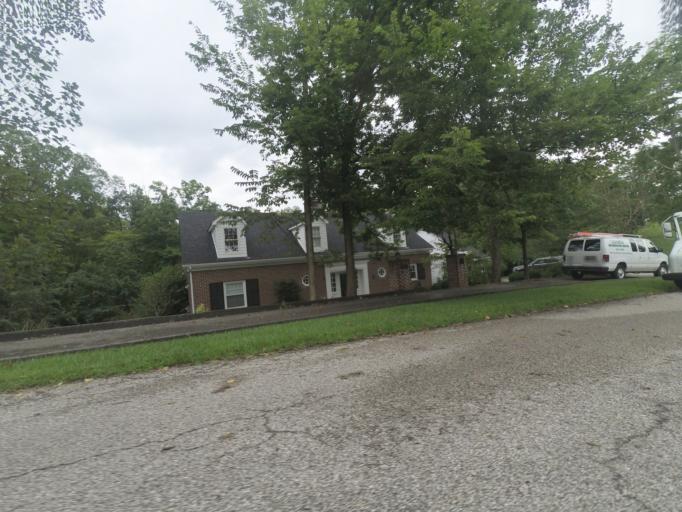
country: US
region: West Virginia
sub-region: Cabell County
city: Huntington
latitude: 38.4037
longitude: -82.4513
